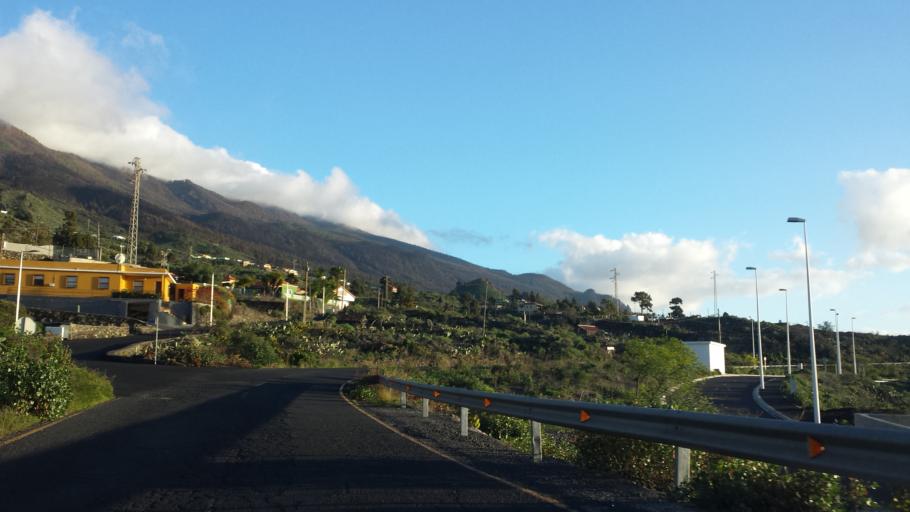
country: ES
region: Canary Islands
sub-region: Provincia de Santa Cruz de Tenerife
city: El Paso
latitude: 28.6254
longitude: -17.8851
